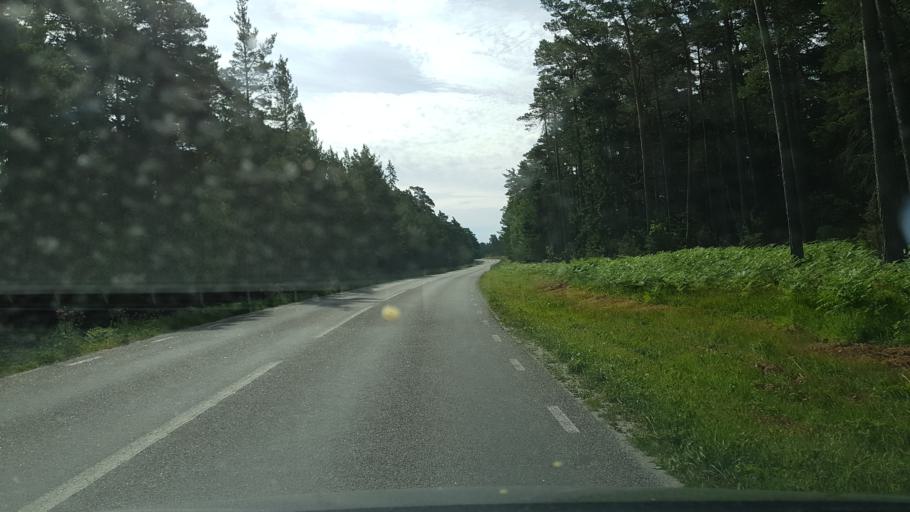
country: SE
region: Gotland
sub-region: Gotland
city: Hemse
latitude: 57.4684
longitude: 18.5633
